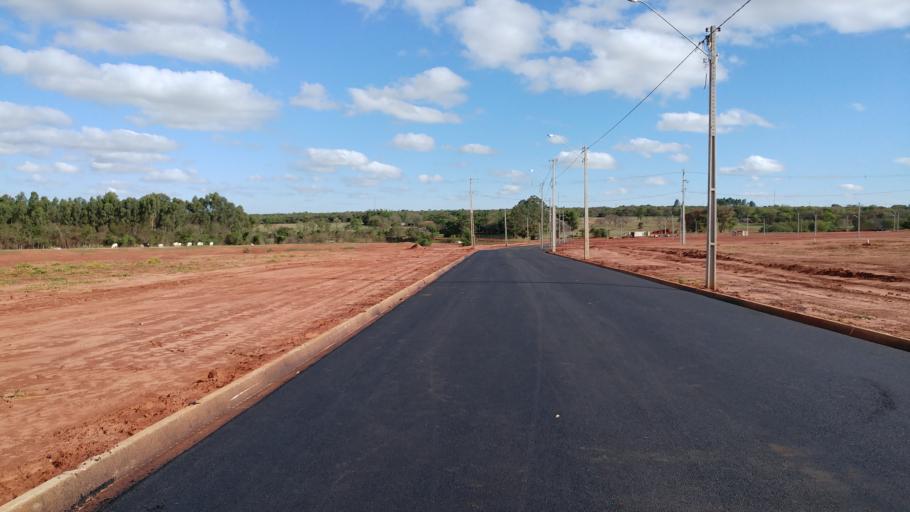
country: BR
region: Sao Paulo
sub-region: Paraguacu Paulista
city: Paraguacu Paulista
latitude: -22.4364
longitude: -50.5749
